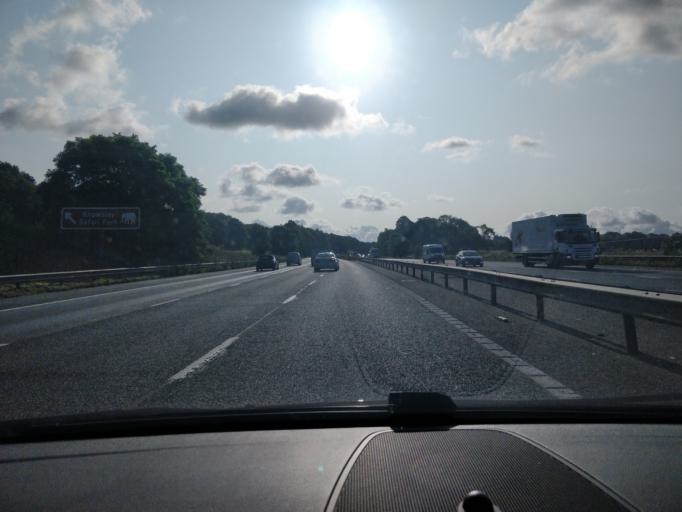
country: GB
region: England
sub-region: Knowsley
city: Huyton
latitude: 53.4302
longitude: -2.8357
